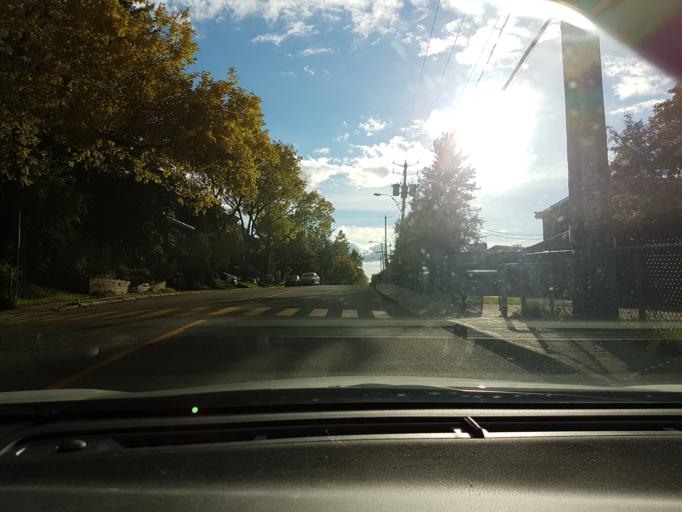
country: CA
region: Quebec
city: Quebec
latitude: 46.7963
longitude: -71.2563
